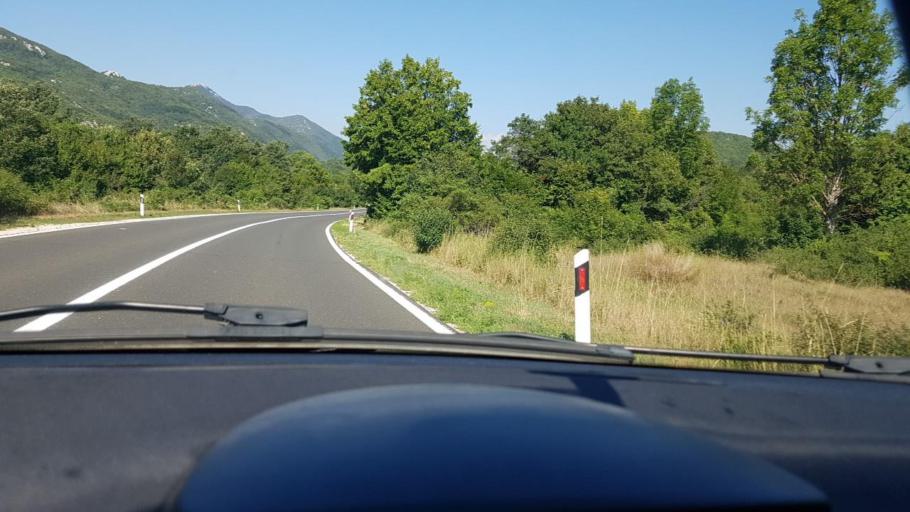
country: HR
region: Zadarska
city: Gracac
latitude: 44.2727
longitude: 15.9196
